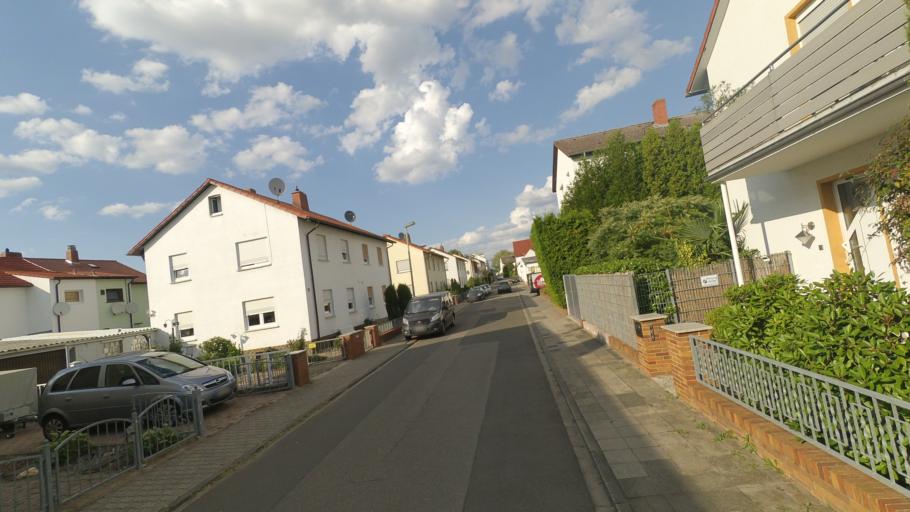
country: DE
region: Hesse
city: Lampertheim
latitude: 49.5953
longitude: 8.4575
